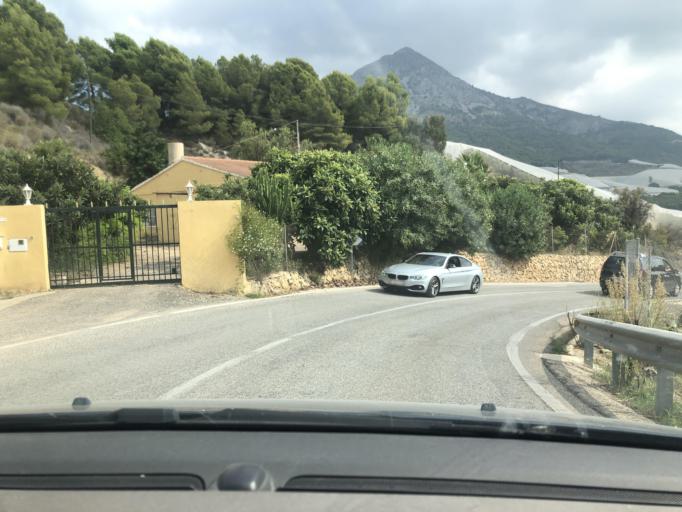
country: ES
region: Valencia
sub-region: Provincia de Alicante
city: Callosa d'En Sarria
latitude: 38.6558
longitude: -0.1050
